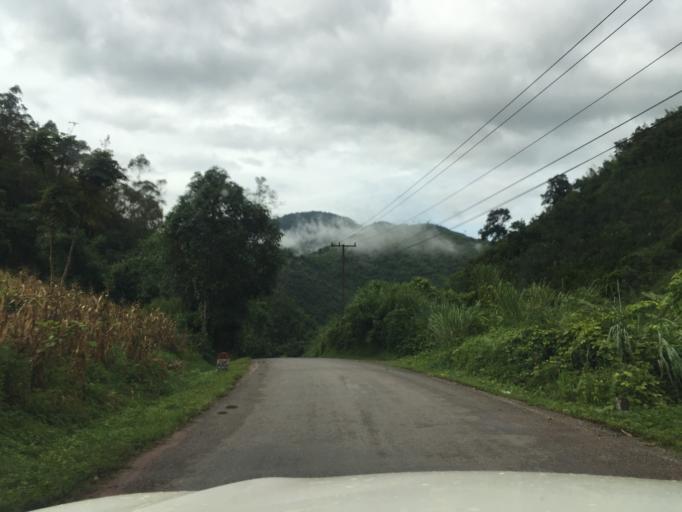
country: LA
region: Oudomxai
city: Muang La
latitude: 20.7967
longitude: 102.0854
